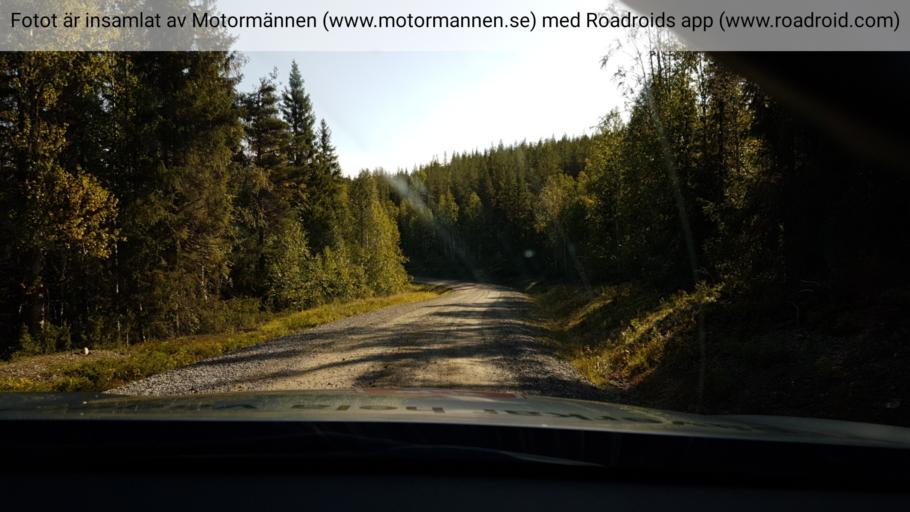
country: SE
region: Vaesterbotten
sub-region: Norsjo Kommun
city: Norsjoe
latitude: 64.7111
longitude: 19.5399
